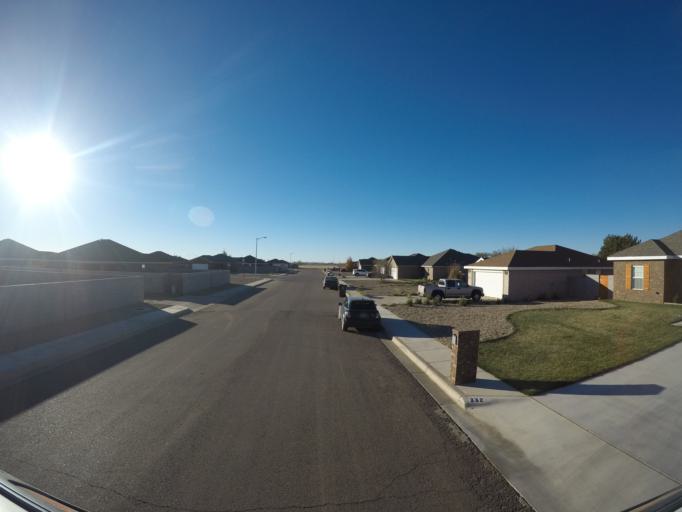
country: US
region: New Mexico
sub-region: Curry County
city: Clovis
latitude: 34.4088
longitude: -103.1733
